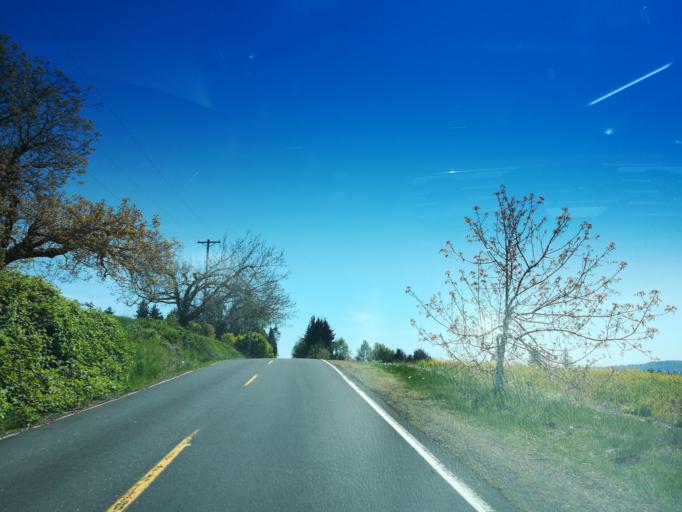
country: US
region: Oregon
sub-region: Multnomah County
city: Troutdale
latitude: 45.5323
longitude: -122.3522
